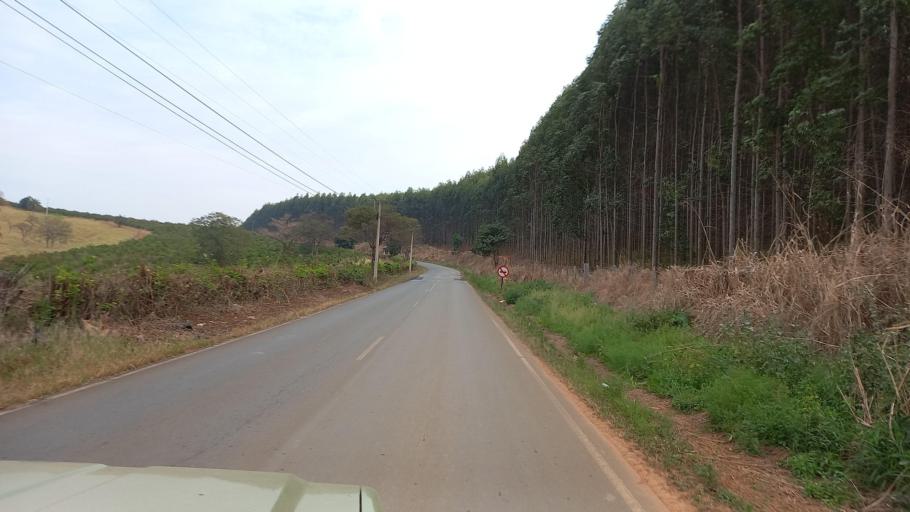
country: BR
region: Sao Paulo
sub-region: Moji-Guacu
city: Mogi-Gaucu
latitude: -22.3294
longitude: -46.8653
